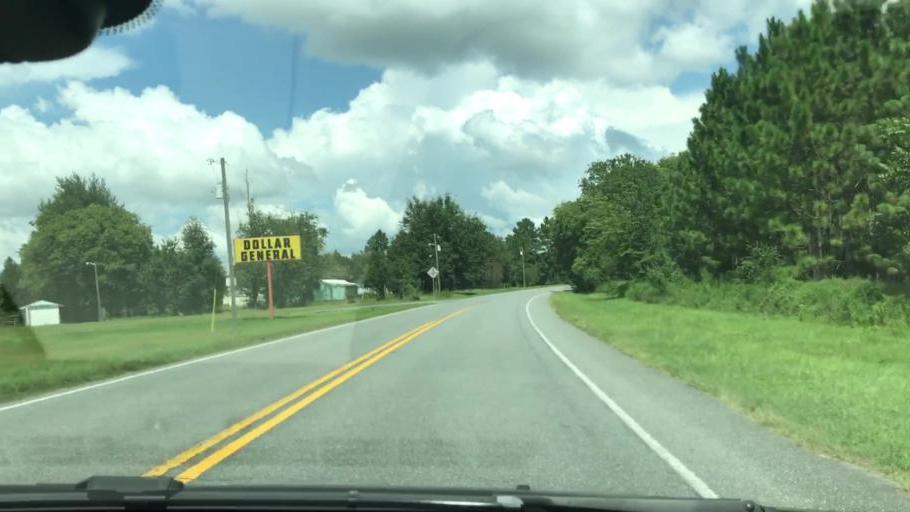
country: US
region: Florida
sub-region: Jackson County
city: Malone
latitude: 30.8819
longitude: -85.1601
